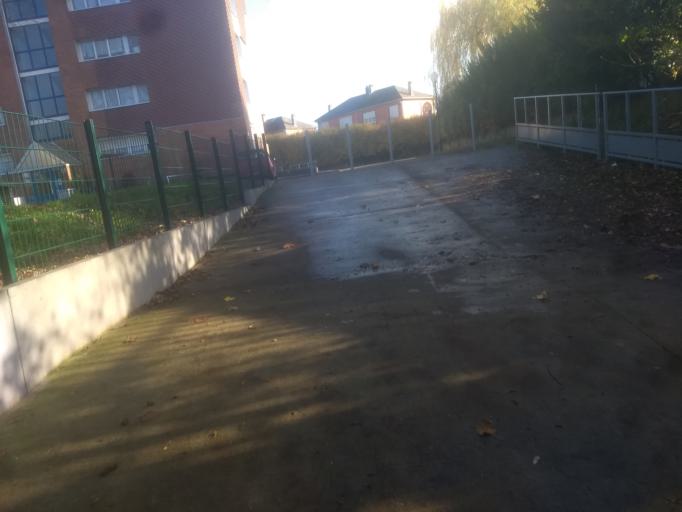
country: FR
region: Nord-Pas-de-Calais
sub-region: Departement du Pas-de-Calais
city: Anzin-Saint-Aubin
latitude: 50.3029
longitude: 2.7430
